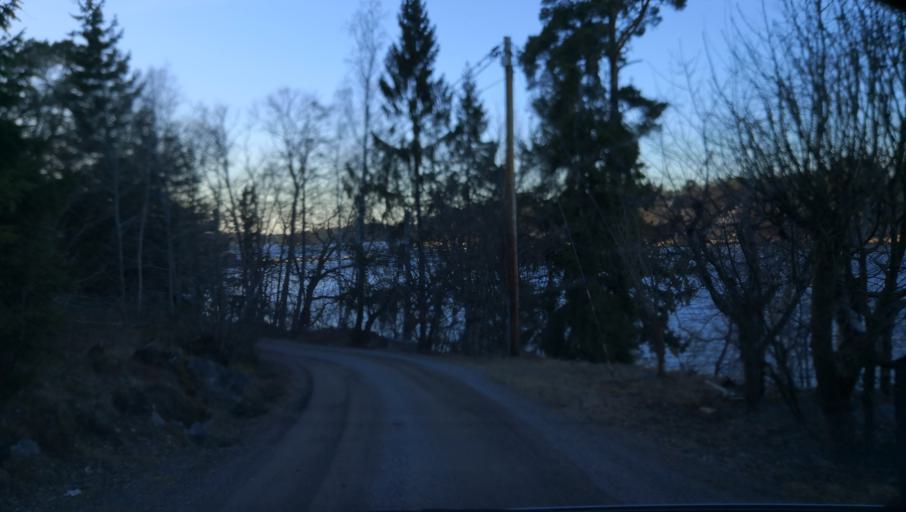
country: SE
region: Stockholm
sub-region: Varmdo Kommun
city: Mortnas
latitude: 59.3366
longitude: 18.4476
